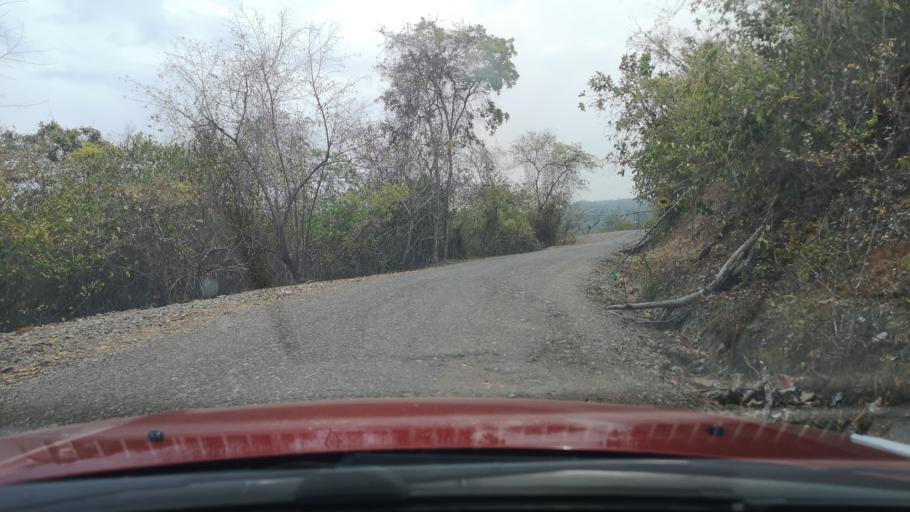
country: CO
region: Huila
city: Neiva
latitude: 2.9563
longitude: -75.3429
